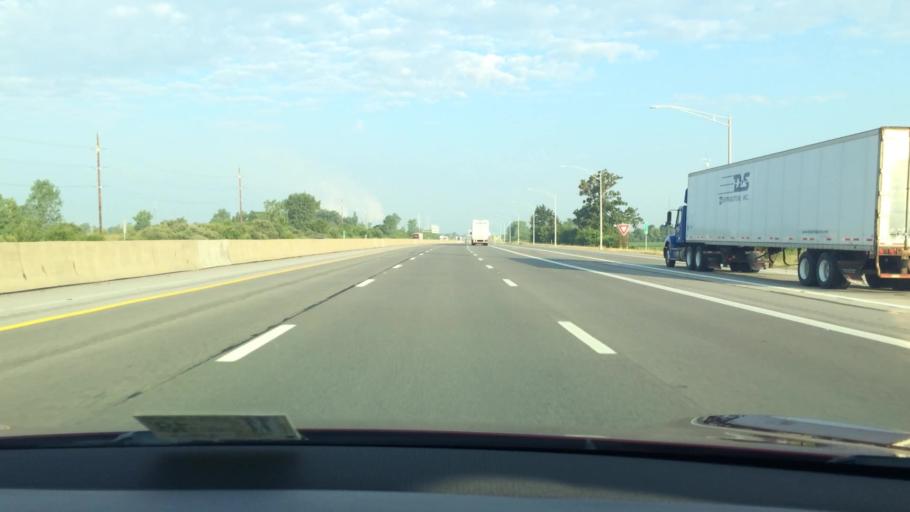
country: US
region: Ohio
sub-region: Huron County
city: Bellevue
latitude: 41.3415
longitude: -82.7692
